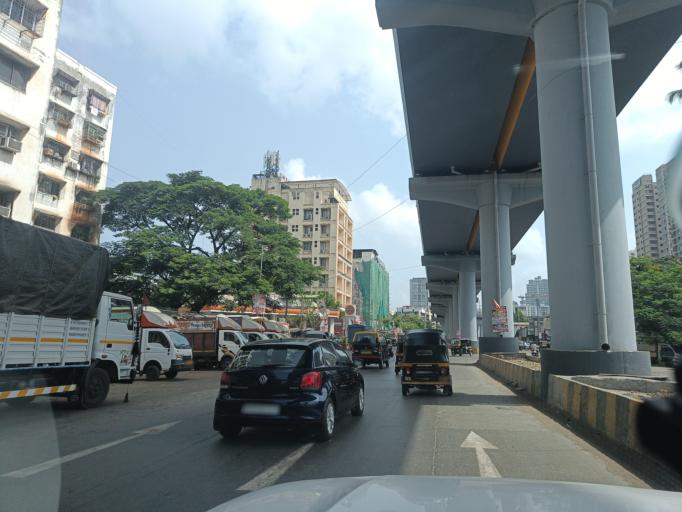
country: IN
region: Maharashtra
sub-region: Mumbai Suburban
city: Powai
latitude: 19.1429
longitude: 72.8312
